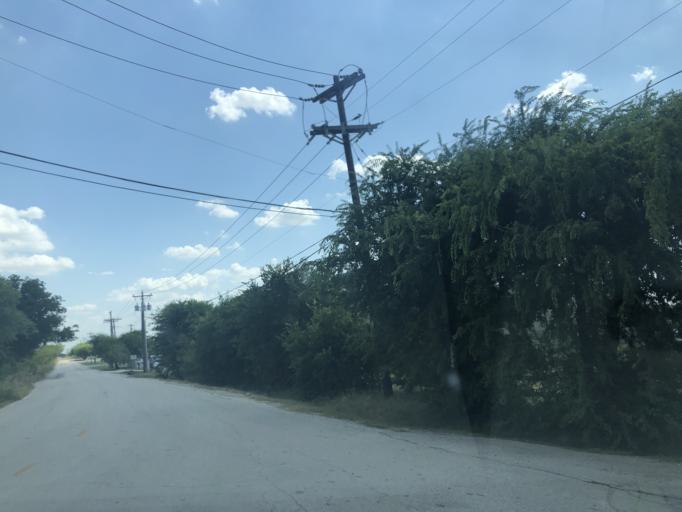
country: US
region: Texas
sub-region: Tarrant County
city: Haslet
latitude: 32.9421
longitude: -97.3226
